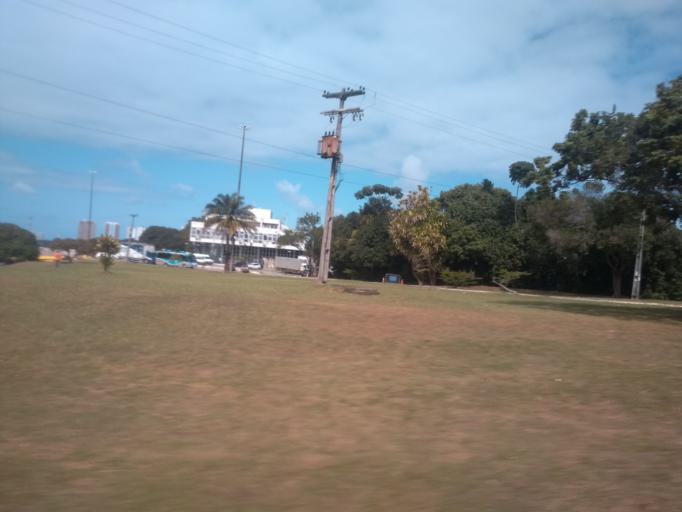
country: BR
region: Bahia
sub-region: Salvador
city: Salvador
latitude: -12.9437
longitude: -38.4236
